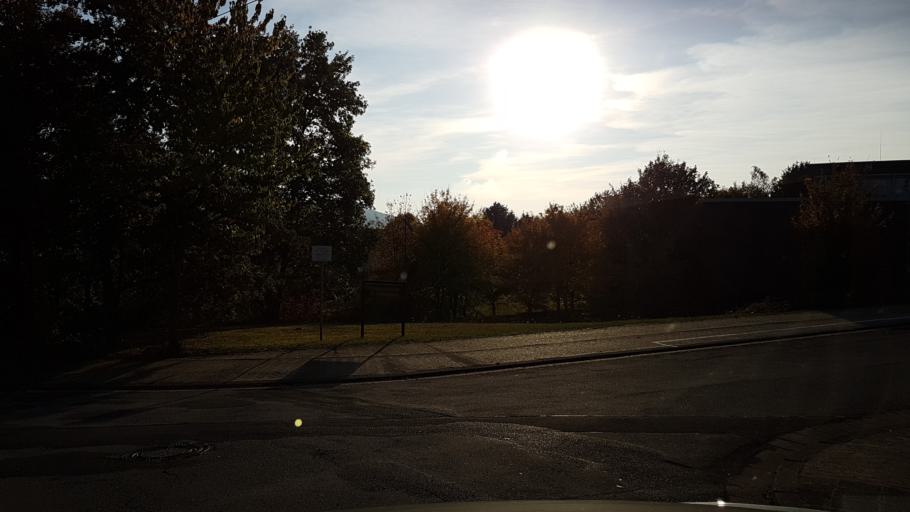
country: DE
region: Saarland
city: Lebach
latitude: 49.4152
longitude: 6.9050
